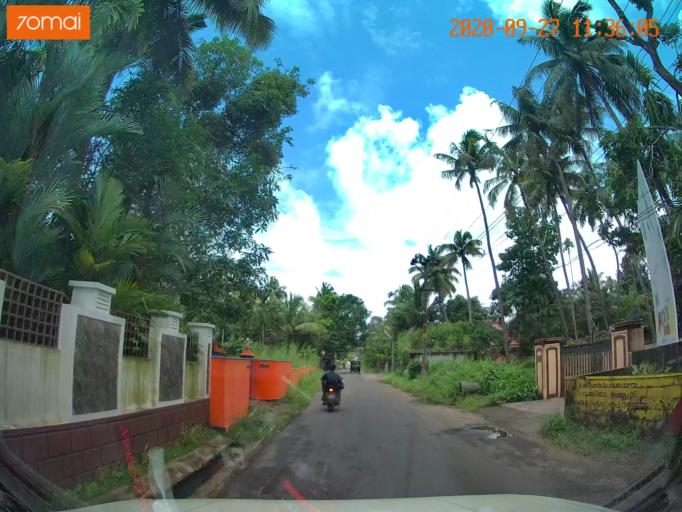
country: IN
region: Kerala
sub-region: Thrissur District
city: Thanniyam
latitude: 10.4471
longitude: 76.1252
